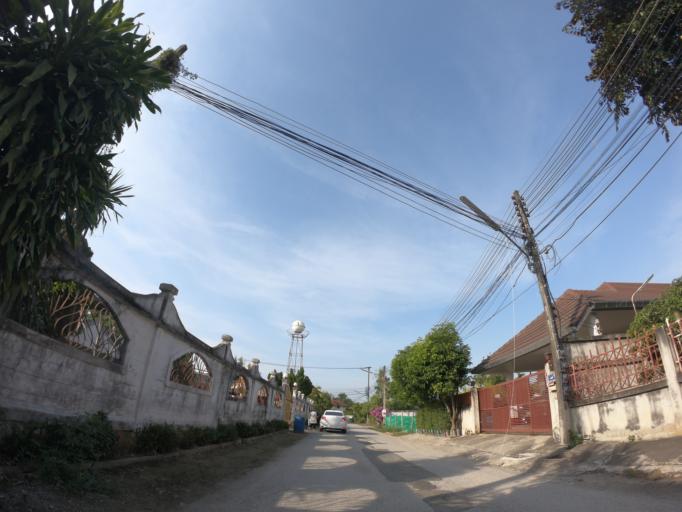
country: TH
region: Chiang Mai
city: Chiang Mai
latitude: 18.8293
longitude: 98.9894
